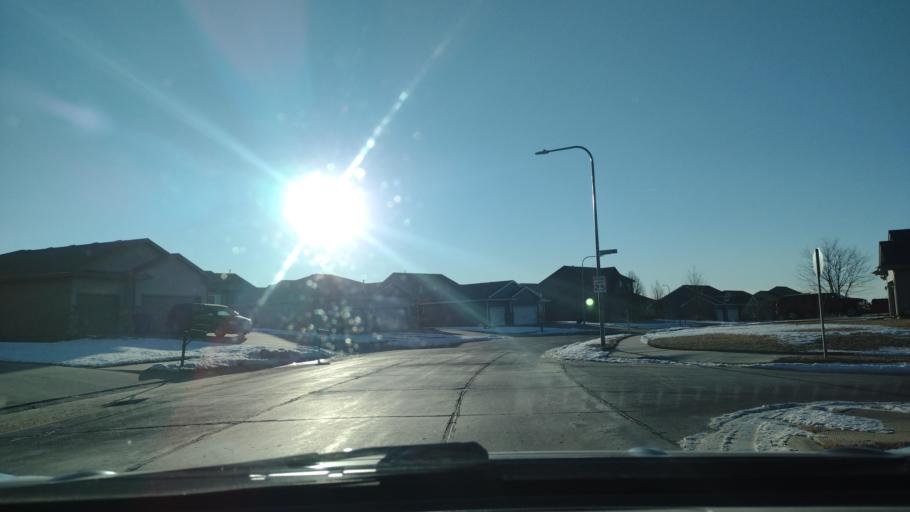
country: US
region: Nebraska
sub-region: Sarpy County
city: Offutt Air Force Base
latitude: 41.0962
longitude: -95.9470
